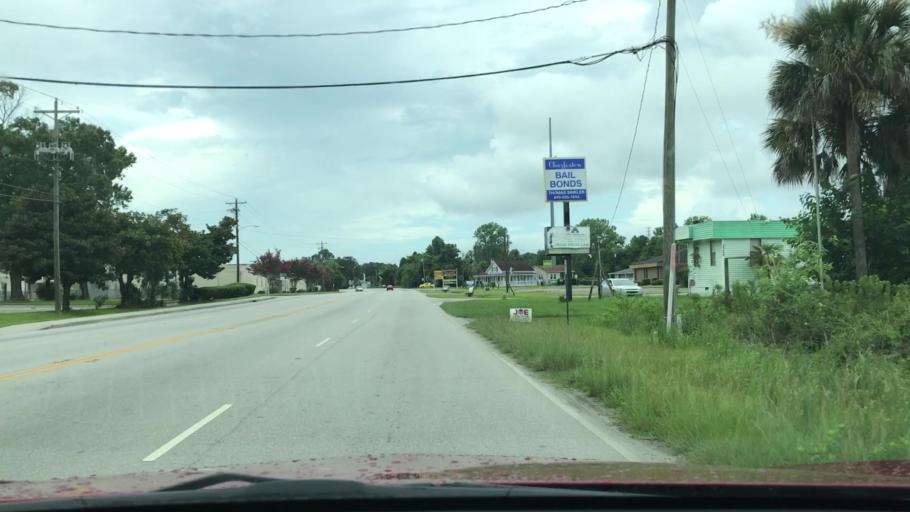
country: US
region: South Carolina
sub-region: Charleston County
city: North Charleston
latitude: 32.8482
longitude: -80.0138
